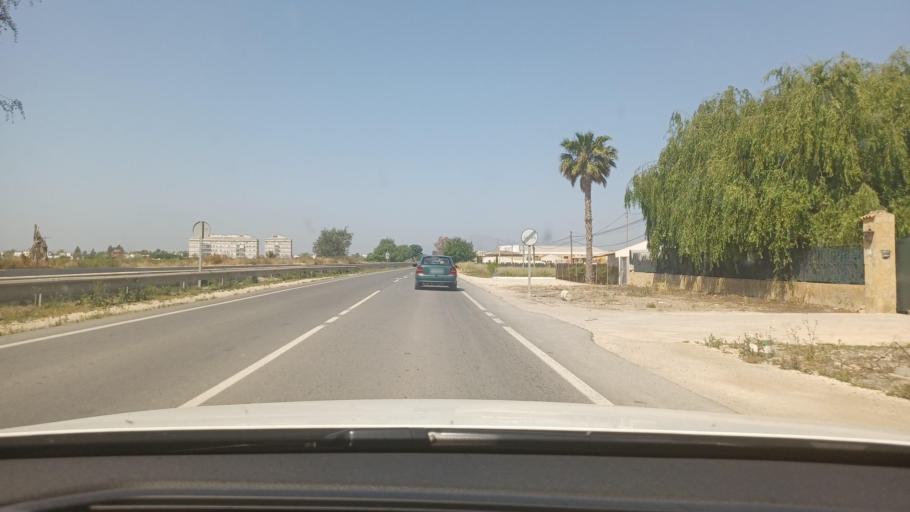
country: ES
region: Valencia
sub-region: Provincia de Alicante
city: Dolores
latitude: 38.1397
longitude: -0.7539
